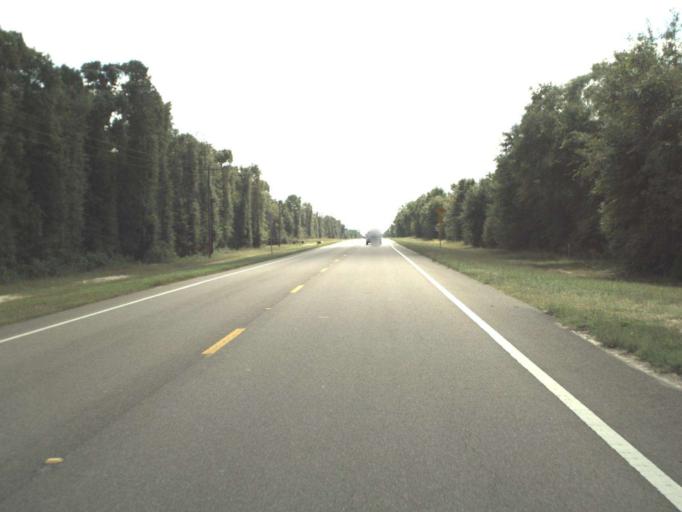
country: US
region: Florida
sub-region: Walton County
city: Freeport
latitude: 30.5706
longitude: -85.9235
